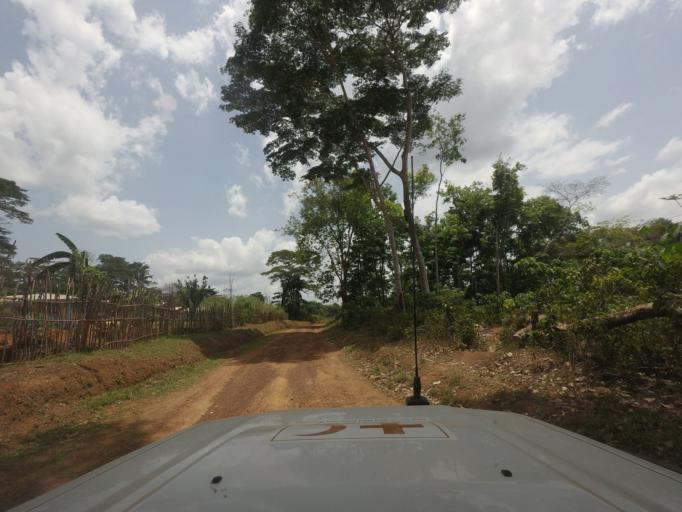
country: LR
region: Bong
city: Gbarnga
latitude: 7.1933
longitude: -9.2062
